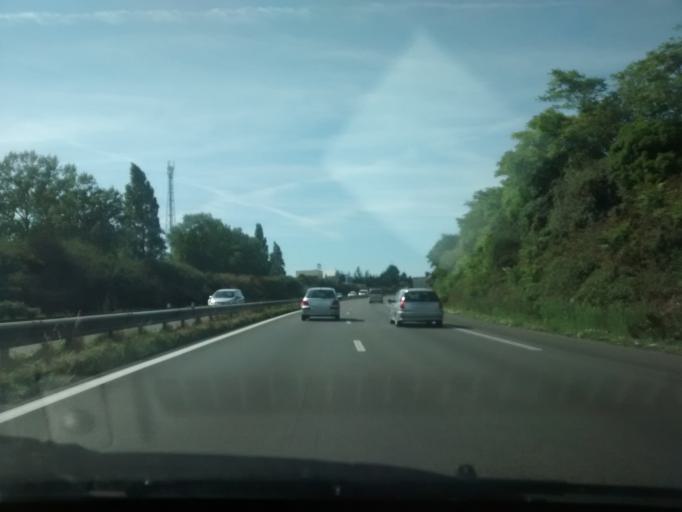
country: FR
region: Brittany
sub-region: Departement des Cotes-d'Armor
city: Langueux
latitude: 48.4866
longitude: -2.7171
